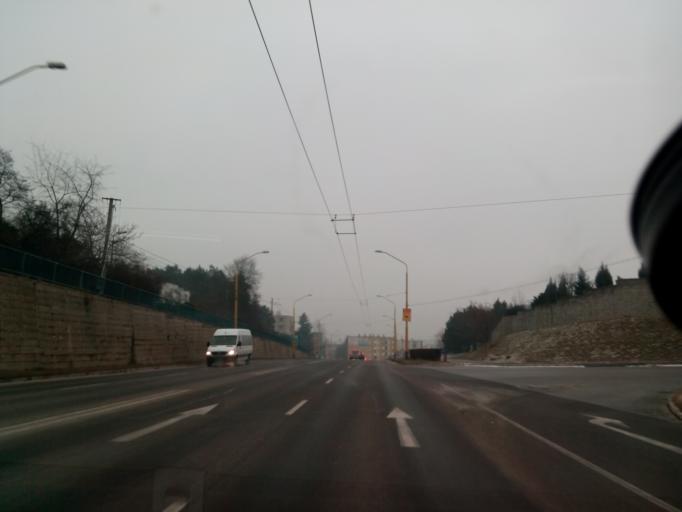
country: SK
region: Kosicky
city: Kosice
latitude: 48.7131
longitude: 21.2231
